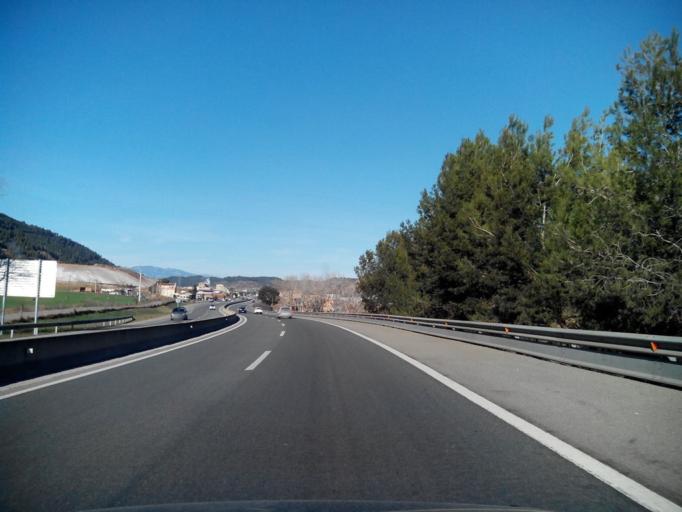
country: ES
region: Catalonia
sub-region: Provincia de Barcelona
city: Sallent
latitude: 41.7960
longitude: 1.8994
